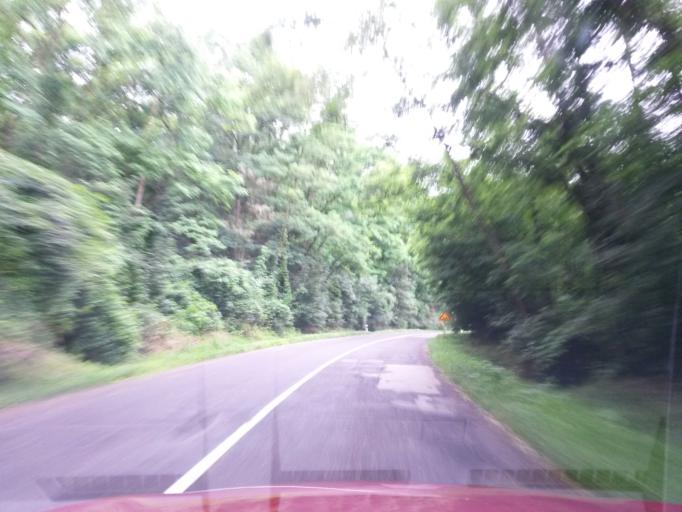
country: SK
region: Banskobystricky
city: Dudince
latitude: 48.1562
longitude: 18.9296
